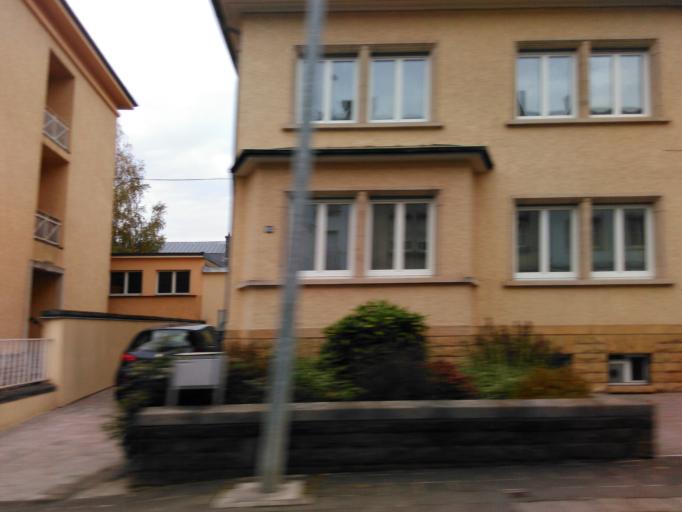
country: LU
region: Luxembourg
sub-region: Canton de Luxembourg
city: Luxembourg
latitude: 49.6201
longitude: 6.1151
